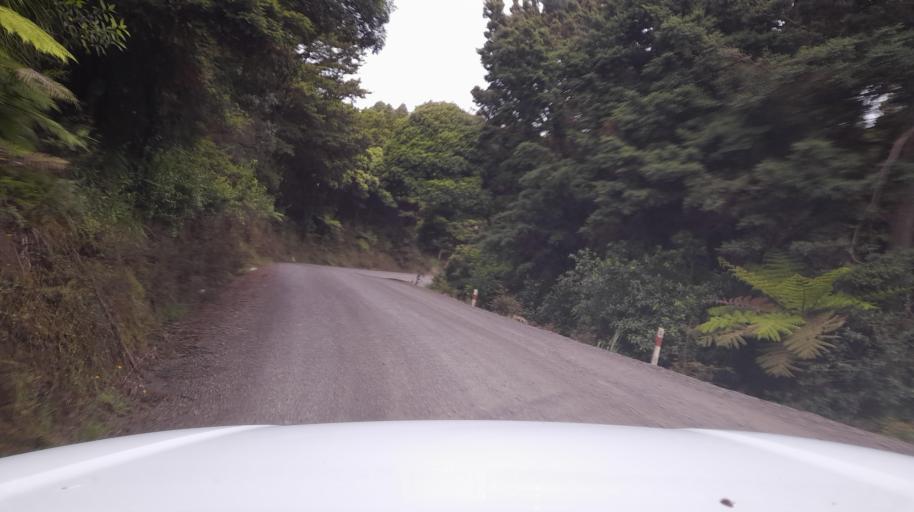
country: NZ
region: Northland
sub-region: Far North District
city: Kaitaia
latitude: -35.3185
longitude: 173.3480
